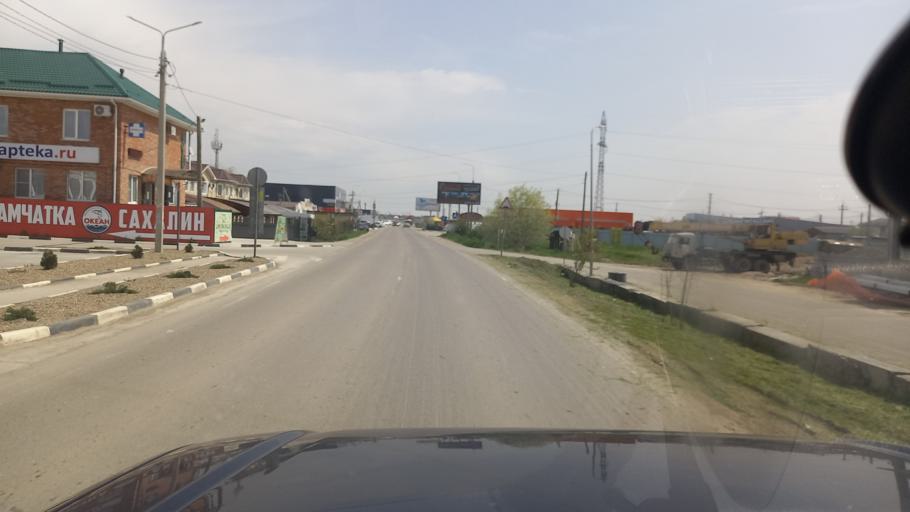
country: RU
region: Adygeya
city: Yablonovskiy
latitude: 44.9859
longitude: 38.9640
